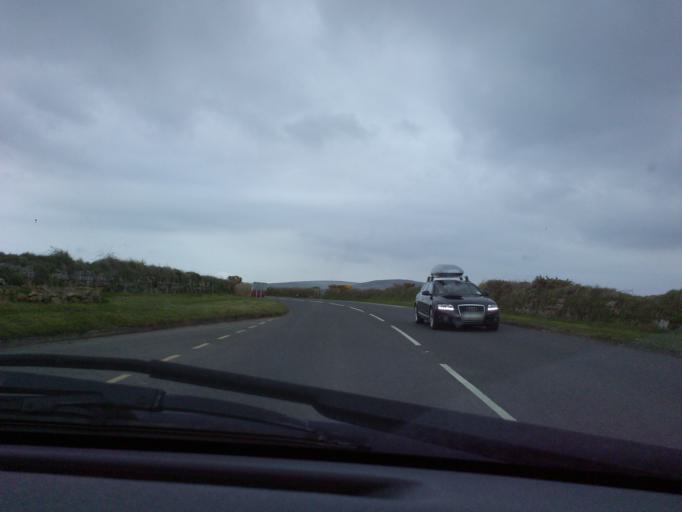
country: GB
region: England
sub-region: Cornwall
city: Sennen
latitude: 50.0799
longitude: -5.6822
